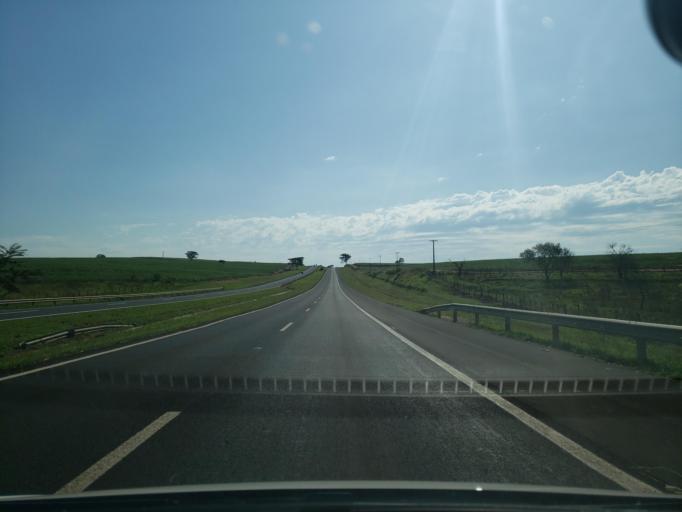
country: BR
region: Sao Paulo
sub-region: Promissao
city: Promissao
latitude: -21.5283
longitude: -49.9883
